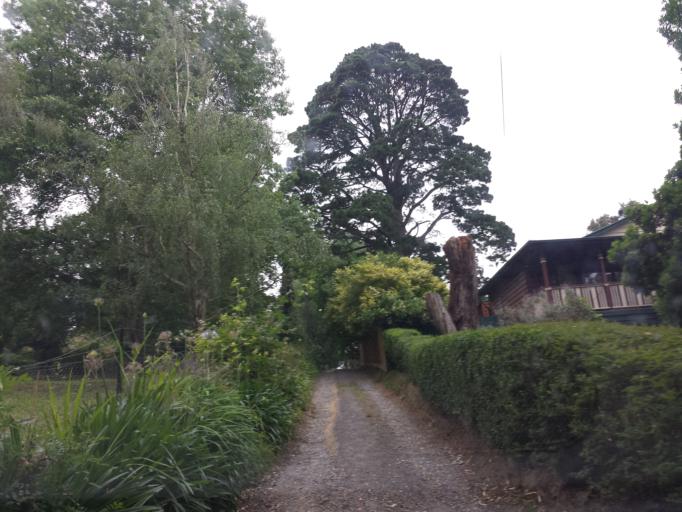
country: AU
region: Victoria
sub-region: Yarra Ranges
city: Tecoma
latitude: -37.9103
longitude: 145.3455
